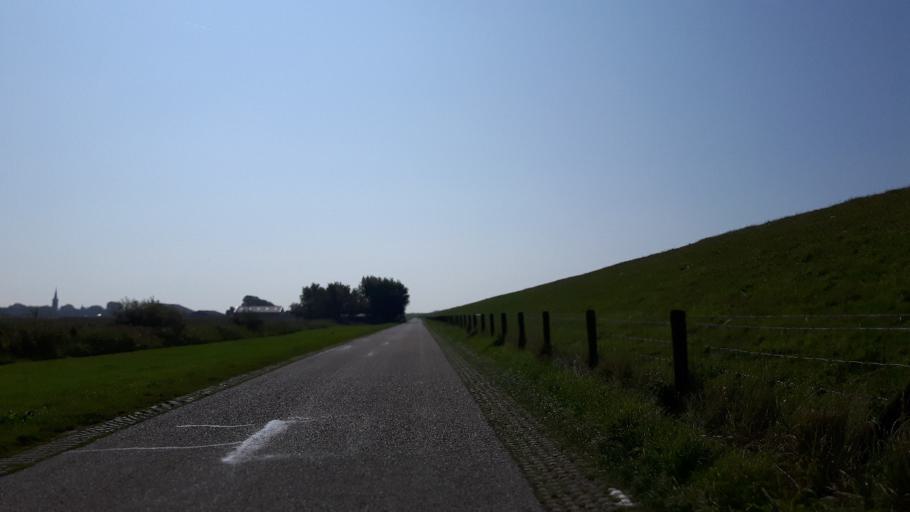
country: NL
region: Friesland
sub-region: Sudwest Fryslan
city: Makkum
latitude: 53.0898
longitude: 5.3809
